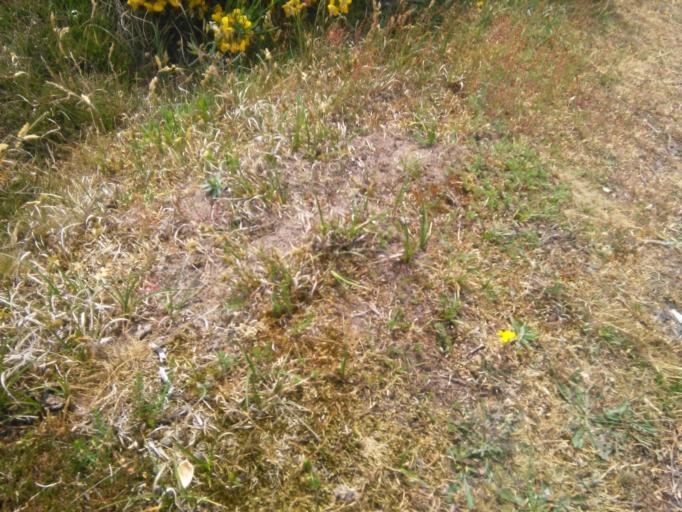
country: DK
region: Capital Region
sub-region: Bornholm Kommune
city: Ronne
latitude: 55.2940
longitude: 14.7777
